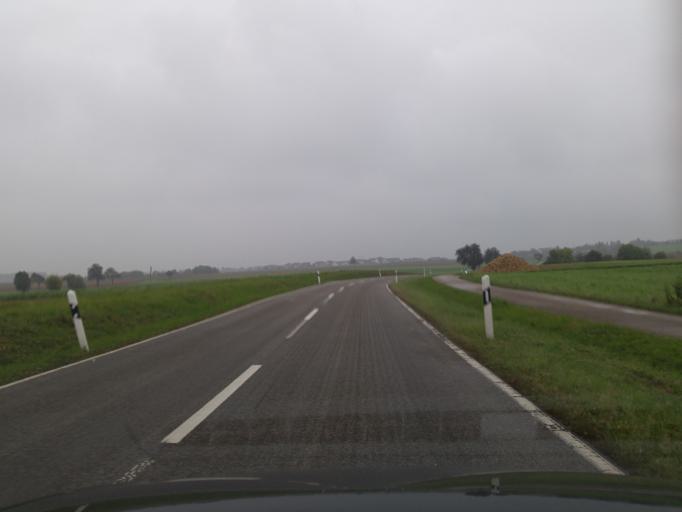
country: DE
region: Baden-Wuerttemberg
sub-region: Regierungsbezirk Stuttgart
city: Bad Wimpfen
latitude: 49.2115
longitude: 9.1487
